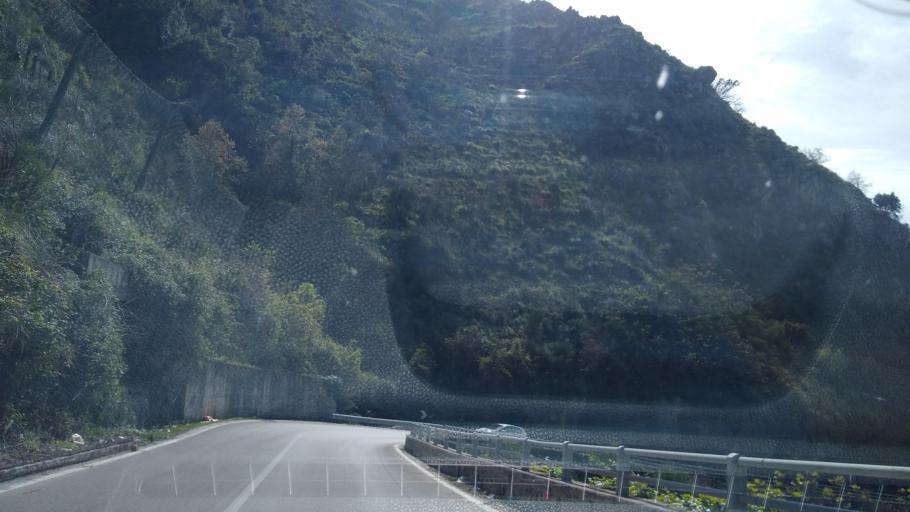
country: IT
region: Sicily
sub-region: Palermo
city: Montelepre
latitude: 38.0502
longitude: 13.1898
